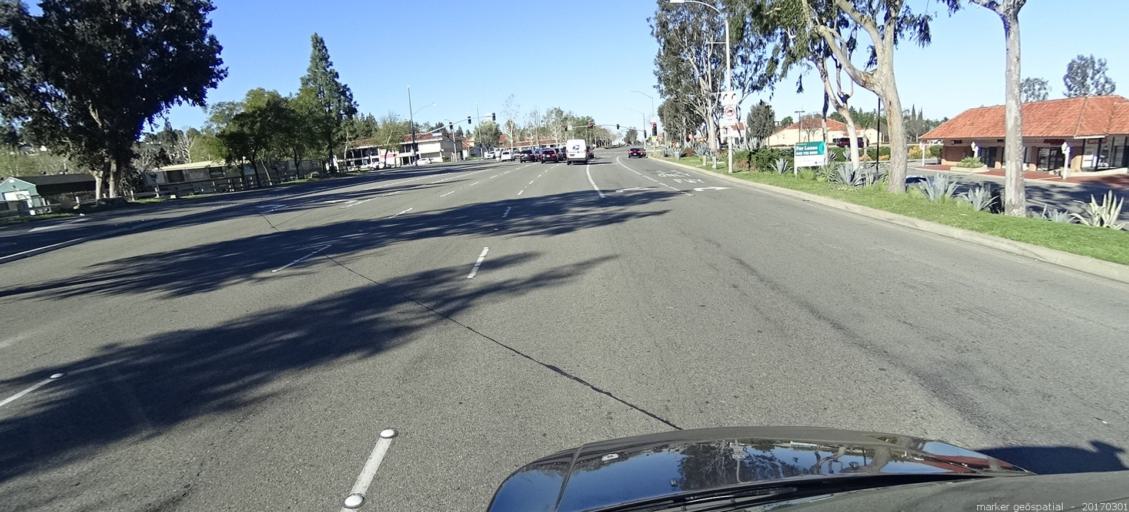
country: US
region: California
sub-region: Orange County
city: Villa Park
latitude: 33.8515
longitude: -117.7893
